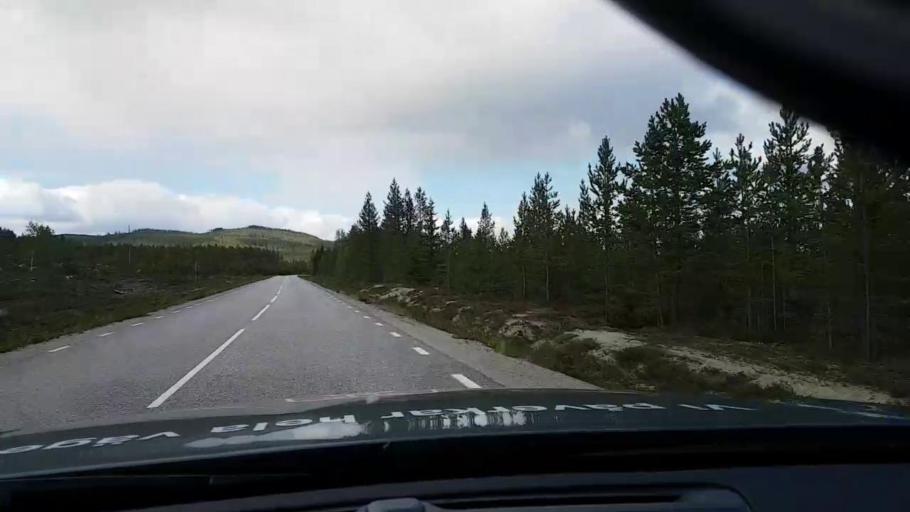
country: SE
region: Vaesternorrland
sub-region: OErnskoeldsviks Kommun
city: Bredbyn
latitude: 63.6783
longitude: 17.7905
